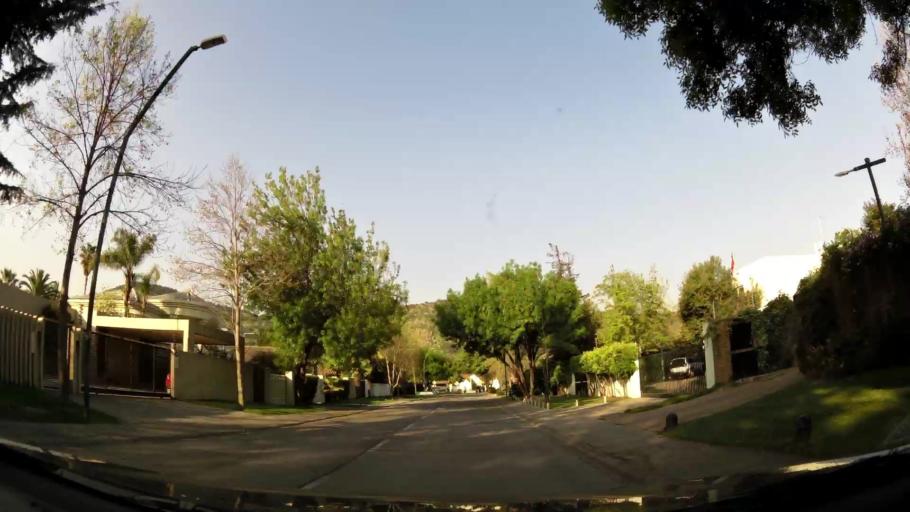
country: CL
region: Santiago Metropolitan
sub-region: Provincia de Santiago
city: Villa Presidente Frei, Nunoa, Santiago, Chile
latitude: -33.3461
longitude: -70.5449
